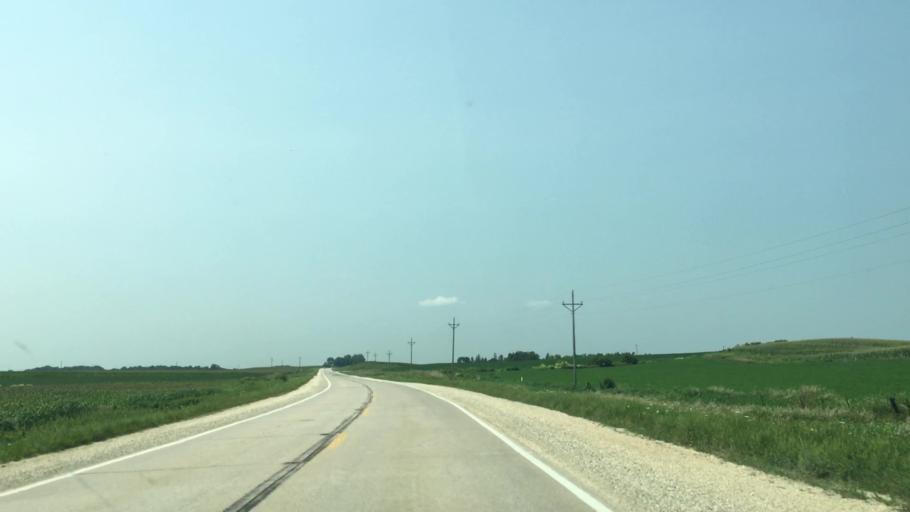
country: US
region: Iowa
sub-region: Fayette County
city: West Union
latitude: 43.0932
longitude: -91.8574
